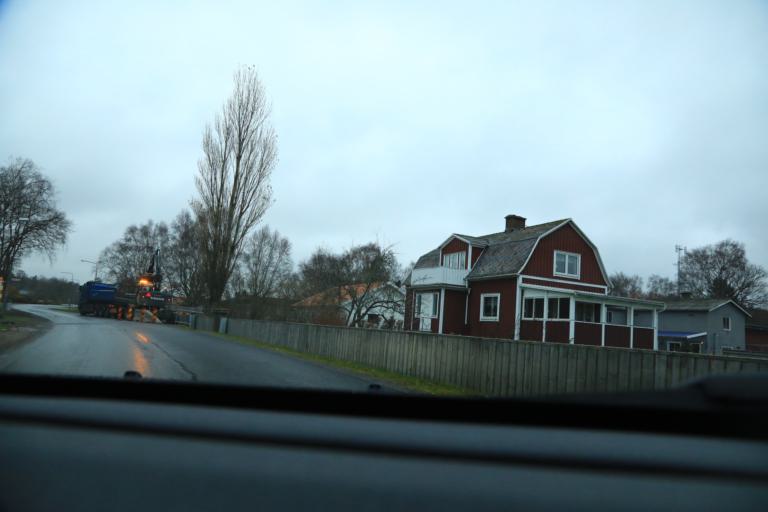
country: SE
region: Halland
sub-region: Varbergs Kommun
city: Varberg
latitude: 57.1735
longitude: 12.2255
